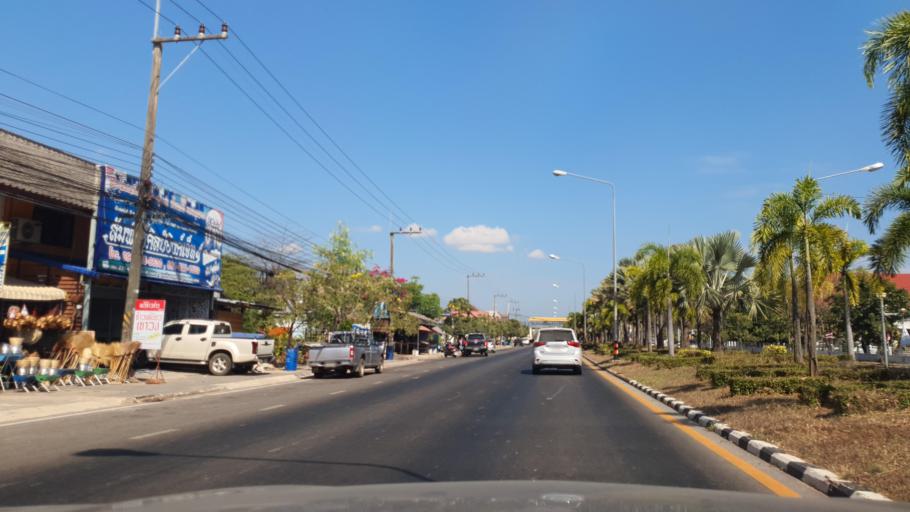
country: TH
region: Kalasin
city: Somdet
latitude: 16.7046
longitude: 103.7486
